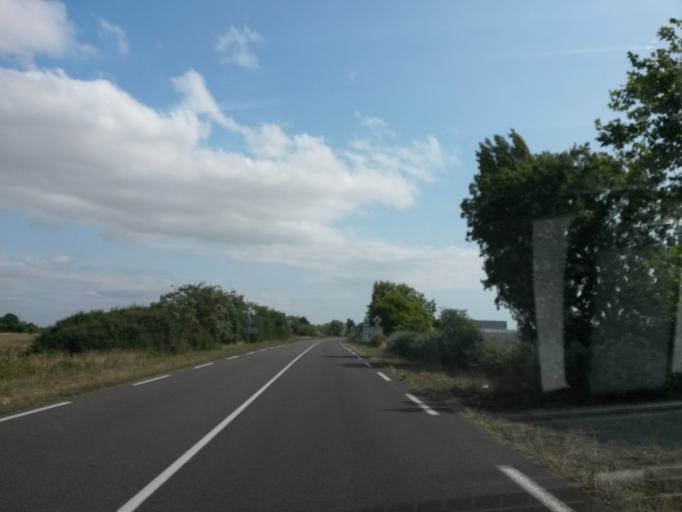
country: FR
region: Pays de la Loire
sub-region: Departement de la Vendee
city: La Tranche-sur-Mer
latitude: 46.3547
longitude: -1.4362
